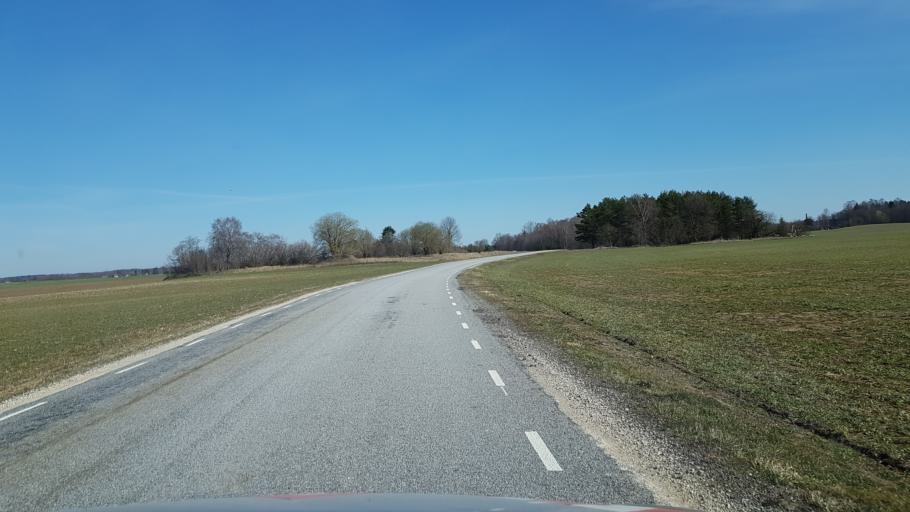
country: EE
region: Laeaene-Virumaa
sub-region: Vinni vald
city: Vinni
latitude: 59.2746
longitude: 26.3750
